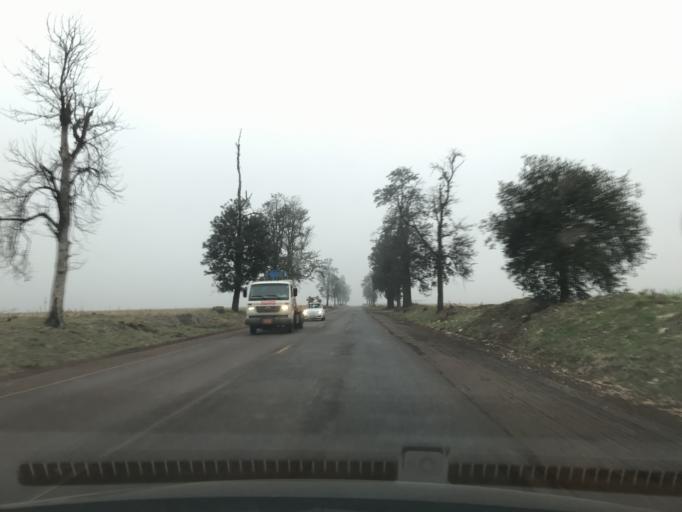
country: BR
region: Parana
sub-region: Palotina
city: Palotina
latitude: -24.4008
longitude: -53.8555
